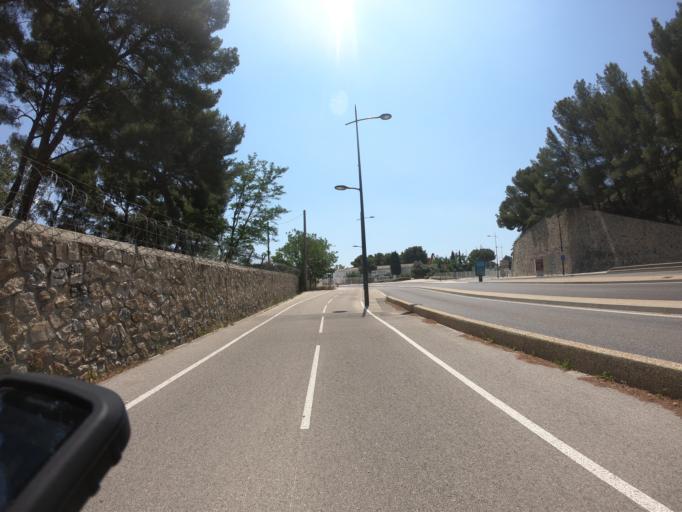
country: FR
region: Provence-Alpes-Cote d'Azur
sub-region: Departement du Var
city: La Seyne-sur-Mer
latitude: 43.1137
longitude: 5.8835
